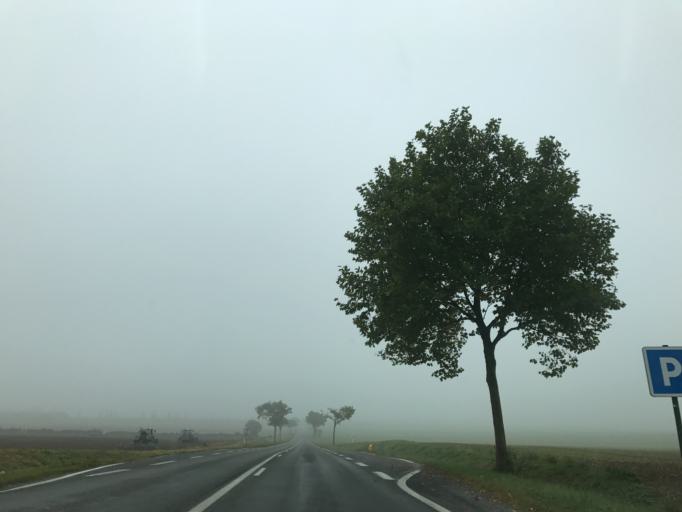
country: FR
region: Picardie
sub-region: Departement de la Somme
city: Moislains
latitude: 50.0461
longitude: 2.9089
